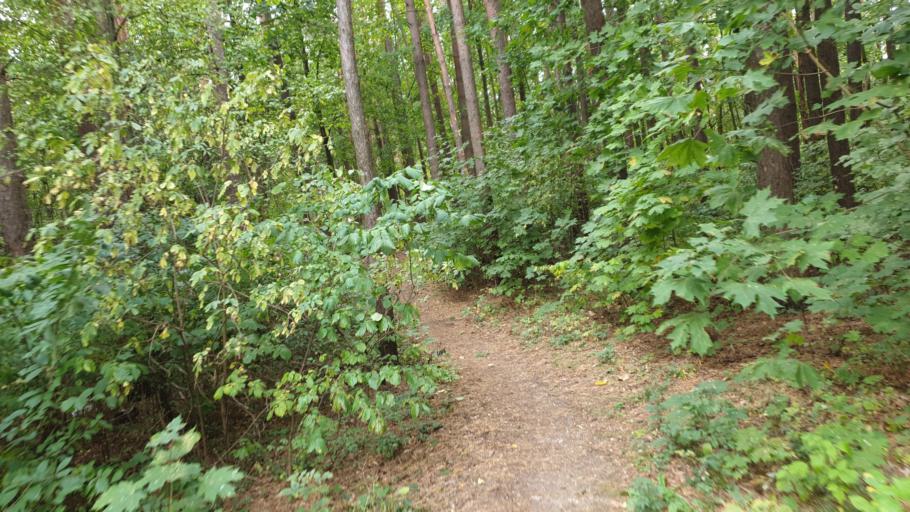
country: LT
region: Vilnius County
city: Seskine
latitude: 54.6987
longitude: 25.2355
